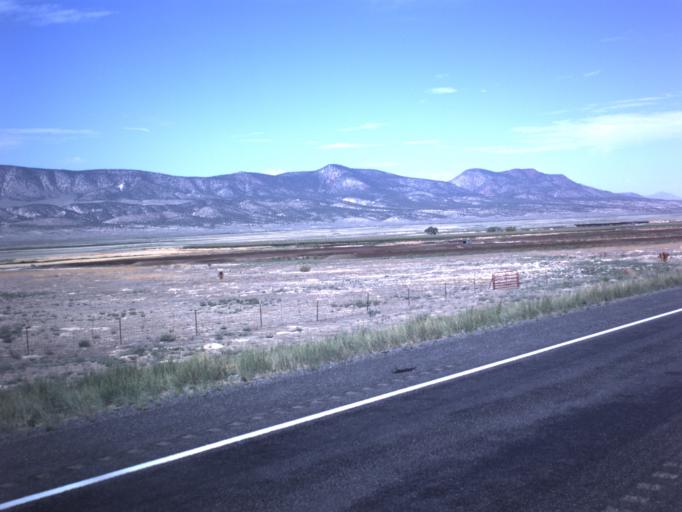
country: US
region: Utah
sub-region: Sanpete County
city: Gunnison
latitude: 39.2494
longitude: -111.8569
